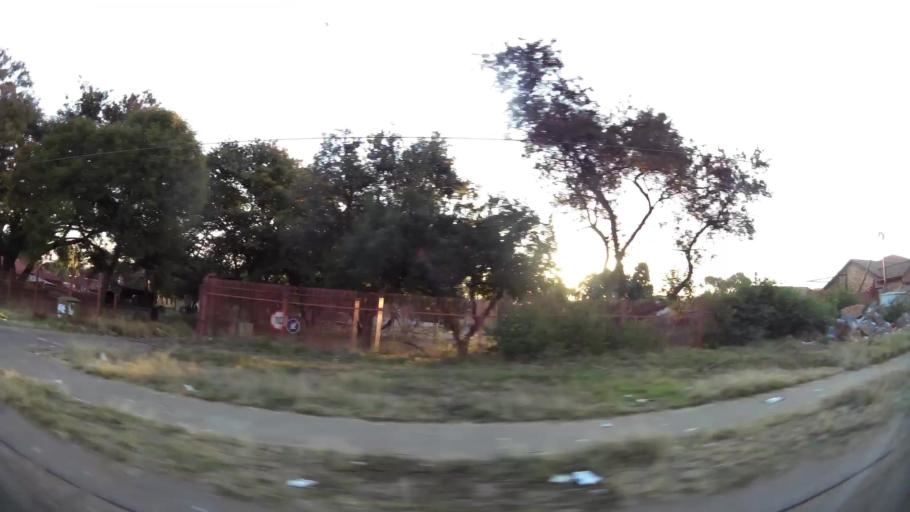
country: ZA
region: Gauteng
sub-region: City of Tshwane Metropolitan Municipality
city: Pretoria
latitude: -25.7401
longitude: 28.1377
